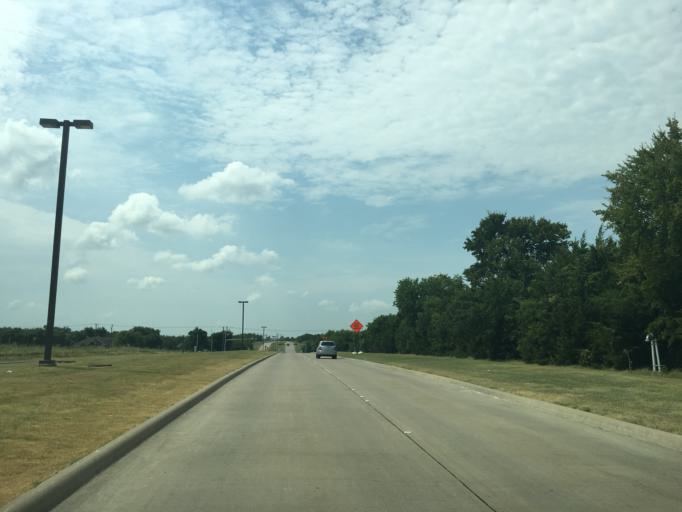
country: US
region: Texas
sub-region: Rockwall County
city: Rockwall
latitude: 32.9680
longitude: -96.4526
